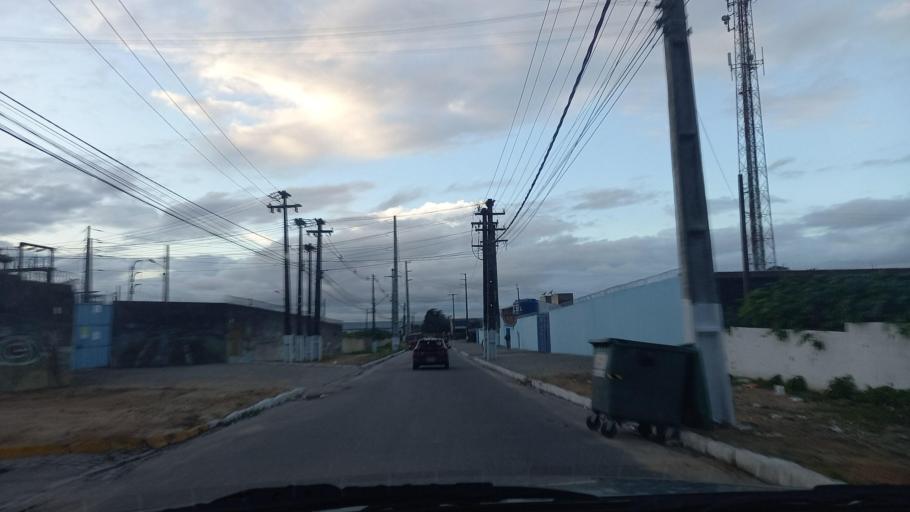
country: BR
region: Pernambuco
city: Garanhuns
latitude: -8.8766
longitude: -36.4655
